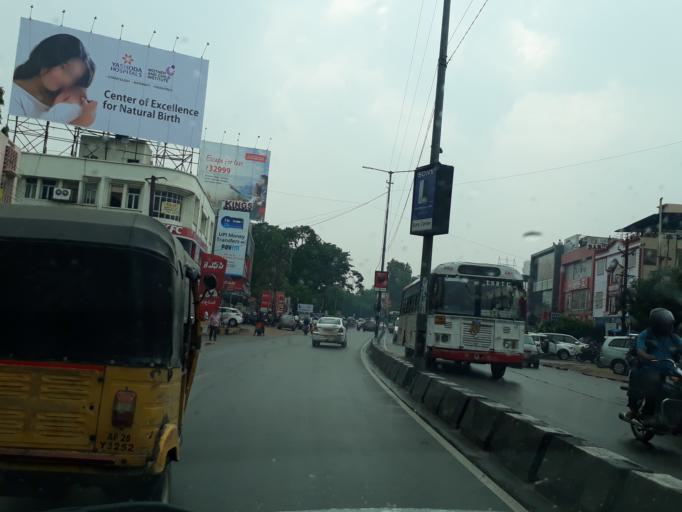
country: IN
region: Telangana
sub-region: Hyderabad
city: Malkajgiri
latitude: 17.4573
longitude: 78.4996
